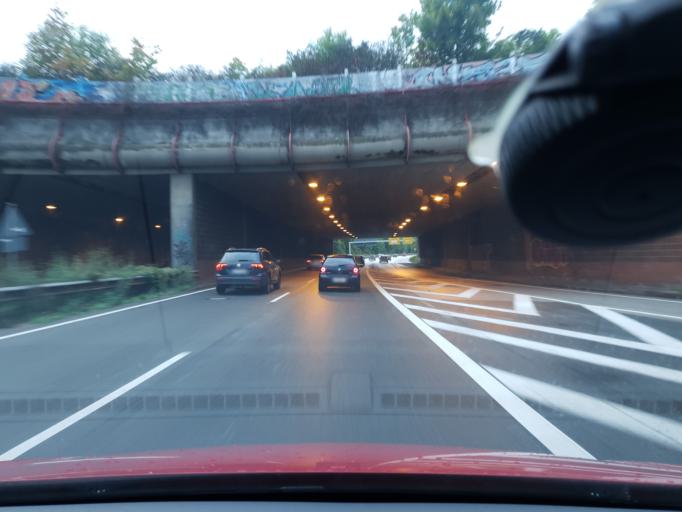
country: DE
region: Schleswig-Holstein
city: Kronshagen
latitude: 54.3186
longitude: 10.0993
